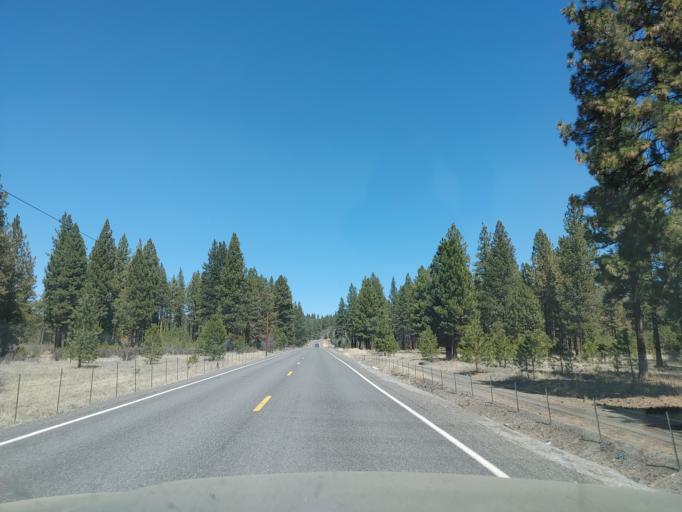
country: US
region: Oregon
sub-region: Klamath County
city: Klamath Falls
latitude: 42.5528
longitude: -121.8956
